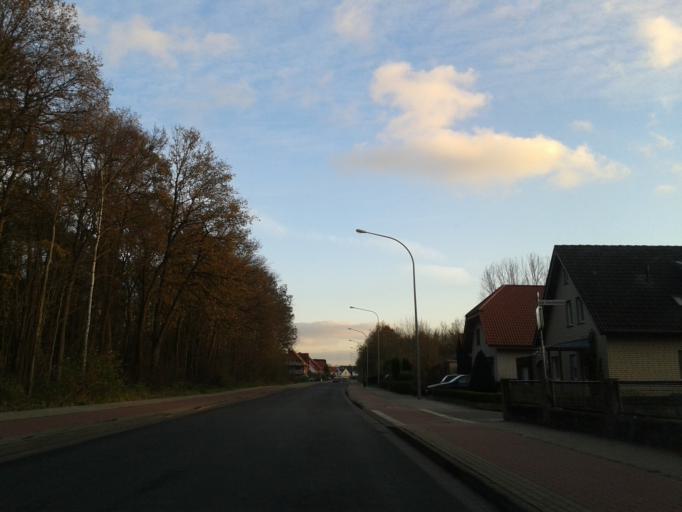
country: DE
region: North Rhine-Westphalia
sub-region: Regierungsbezirk Detmold
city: Paderborn
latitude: 51.7541
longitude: 8.7055
